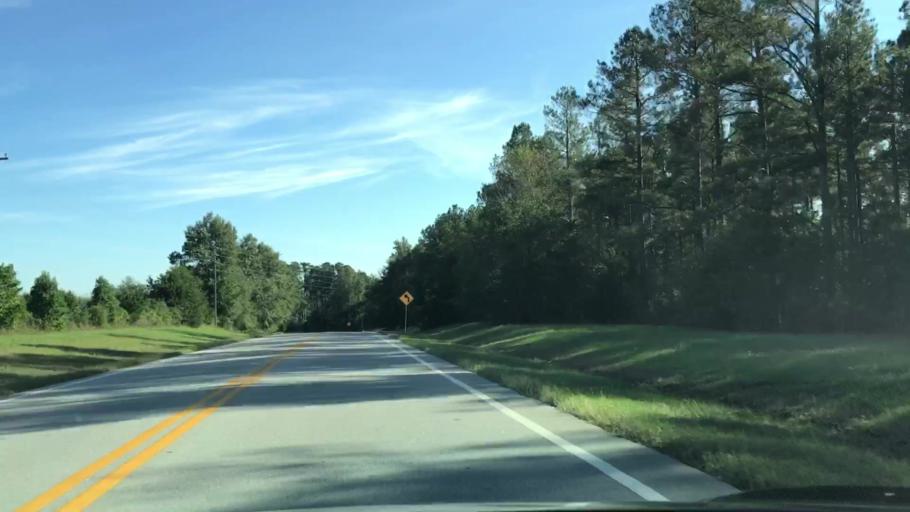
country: US
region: Georgia
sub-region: Glascock County
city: Gibson
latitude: 33.3243
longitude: -82.5589
